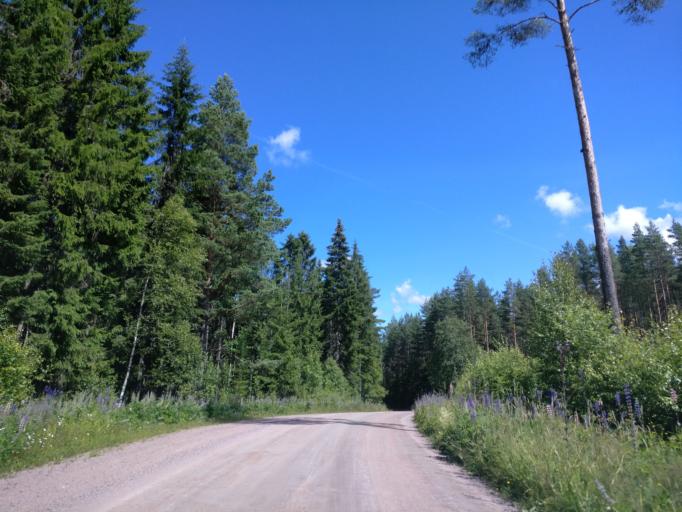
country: SE
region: Vaermland
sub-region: Hagfors Kommun
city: Hagfors
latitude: 60.0420
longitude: 13.6563
